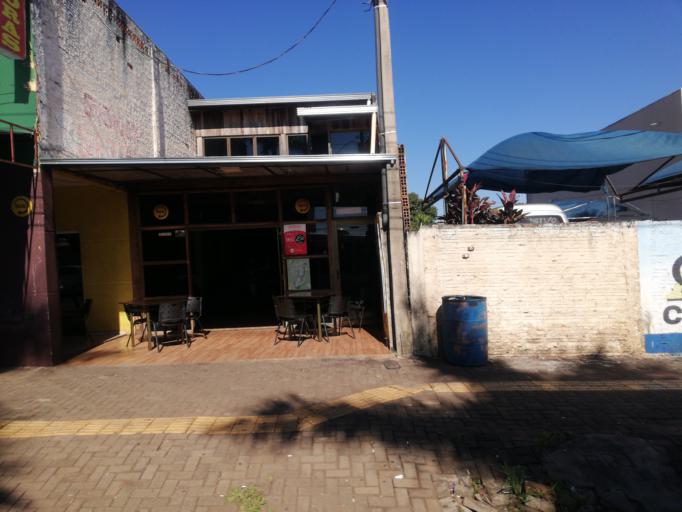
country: BR
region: Parana
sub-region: Foz Do Iguacu
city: Foz do Iguacu
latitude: -25.5526
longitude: -54.5704
